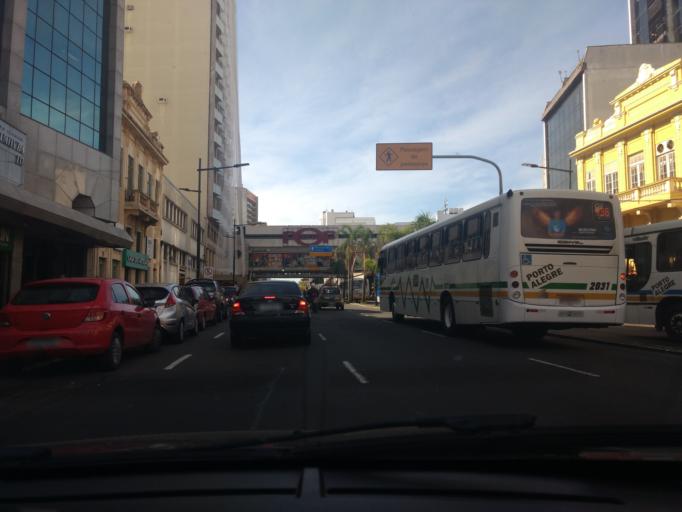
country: BR
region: Rio Grande do Sul
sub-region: Porto Alegre
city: Porto Alegre
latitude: -30.0263
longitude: -51.2257
